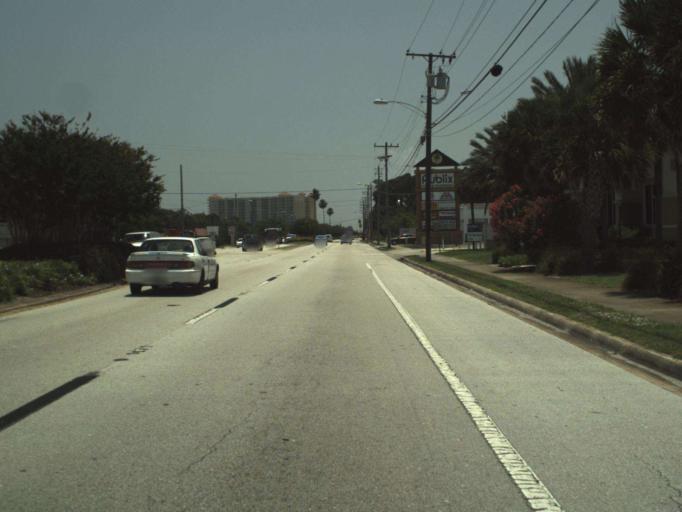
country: US
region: Florida
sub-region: Volusia County
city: South Daytona
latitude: 29.1663
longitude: -80.9991
